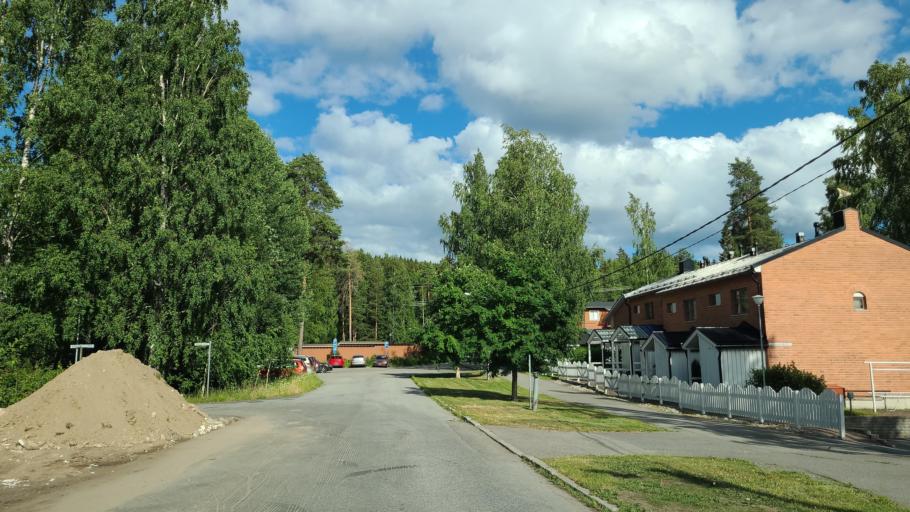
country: FI
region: Northern Savo
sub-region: Kuopio
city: Kuopio
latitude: 62.9255
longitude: 27.6331
